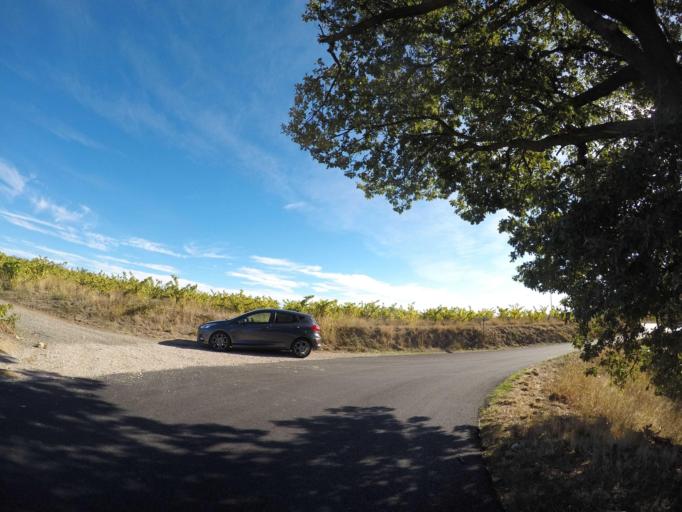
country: FR
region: Languedoc-Roussillon
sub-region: Departement des Pyrenees-Orientales
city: Trouillas
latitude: 42.5699
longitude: 2.7953
